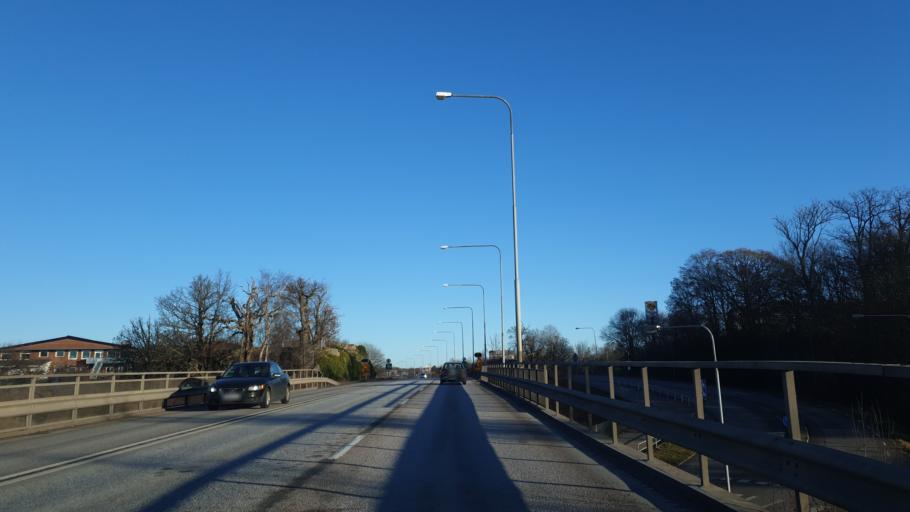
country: SE
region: Blekinge
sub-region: Karlskrona Kommun
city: Karlskrona
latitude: 56.1919
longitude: 15.6256
